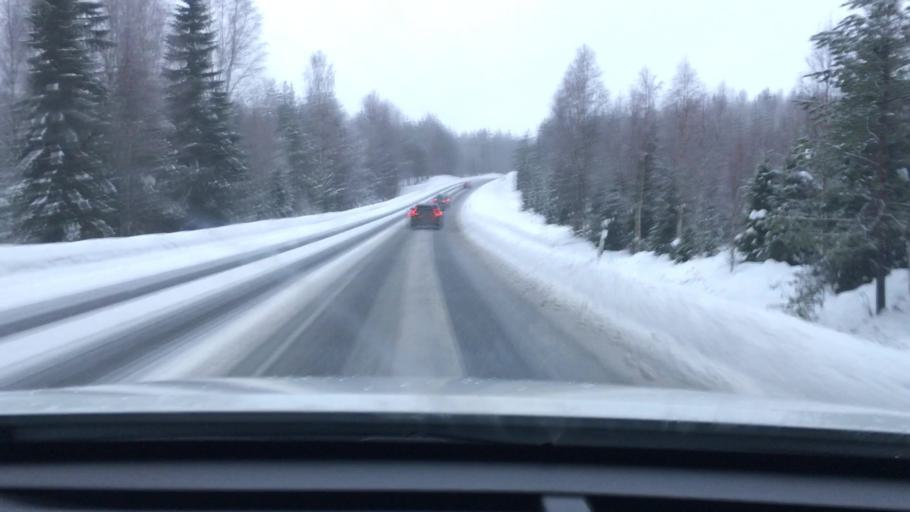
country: FI
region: Northern Savo
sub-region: Ylae-Savo
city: Sonkajaervi
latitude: 63.7690
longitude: 27.4142
